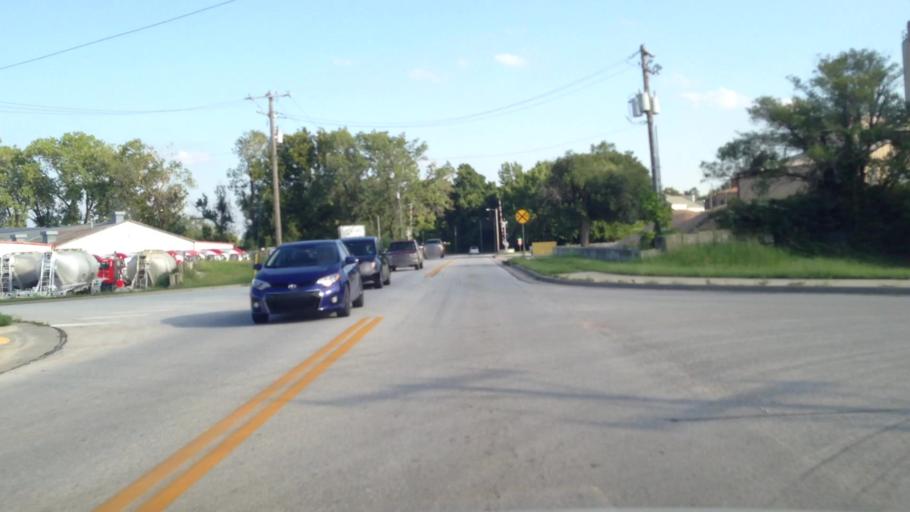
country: US
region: Missouri
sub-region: Jasper County
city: Joplin
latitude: 37.0867
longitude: -94.5063
